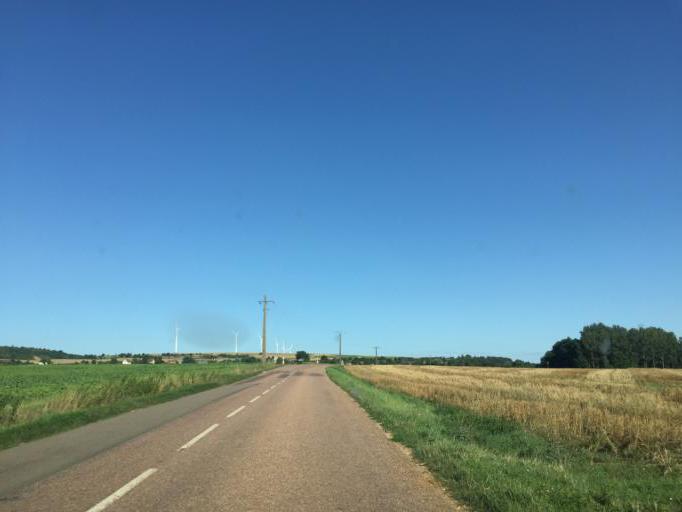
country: FR
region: Bourgogne
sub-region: Departement de l'Yonne
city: Fontenailles
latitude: 47.4774
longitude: 3.4327
